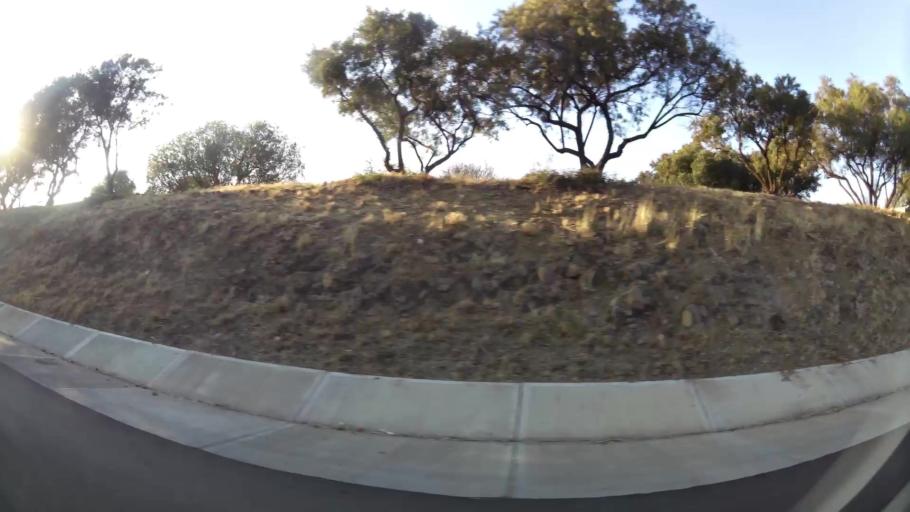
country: ZA
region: Orange Free State
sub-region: Mangaung Metropolitan Municipality
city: Bloemfontein
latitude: -29.0940
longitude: 26.1688
